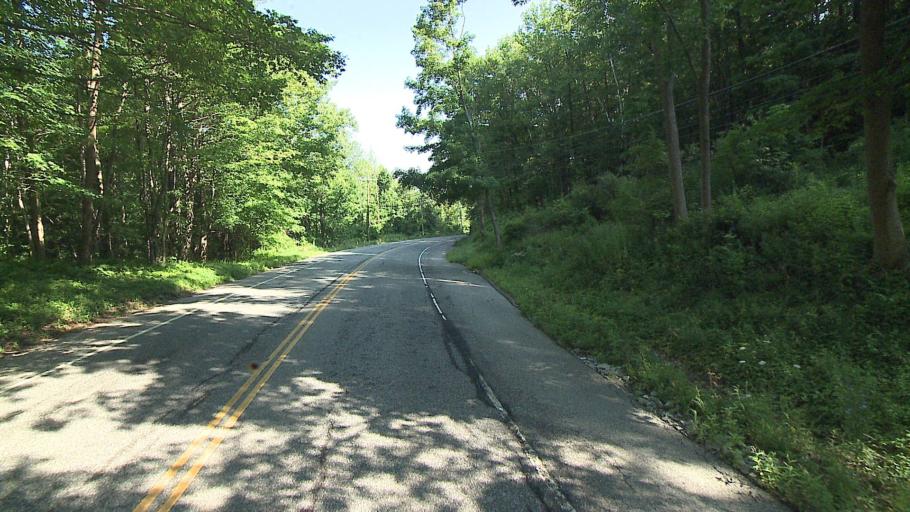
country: US
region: Connecticut
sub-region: Litchfield County
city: Kent
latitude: 41.8455
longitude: -73.4423
